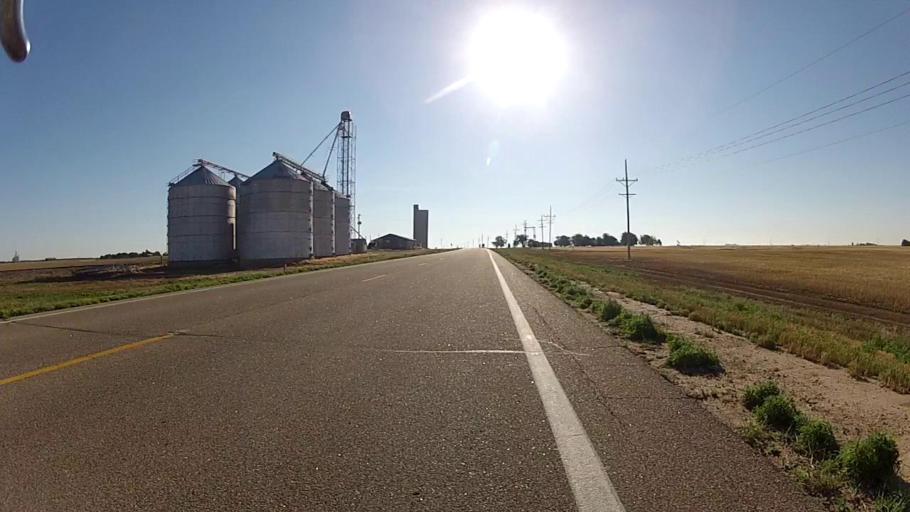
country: US
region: Kansas
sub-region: Haskell County
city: Sublette
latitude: 37.5148
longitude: -100.7303
